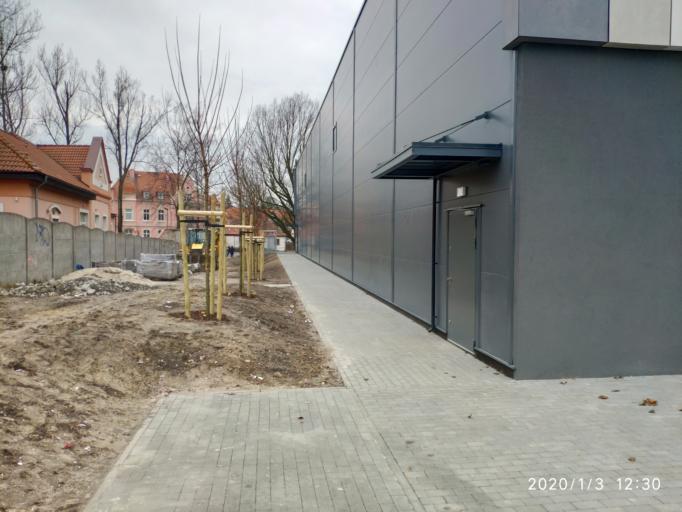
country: PL
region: Lubusz
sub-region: Zielona Gora
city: Zielona Gora
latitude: 51.9361
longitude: 15.5169
